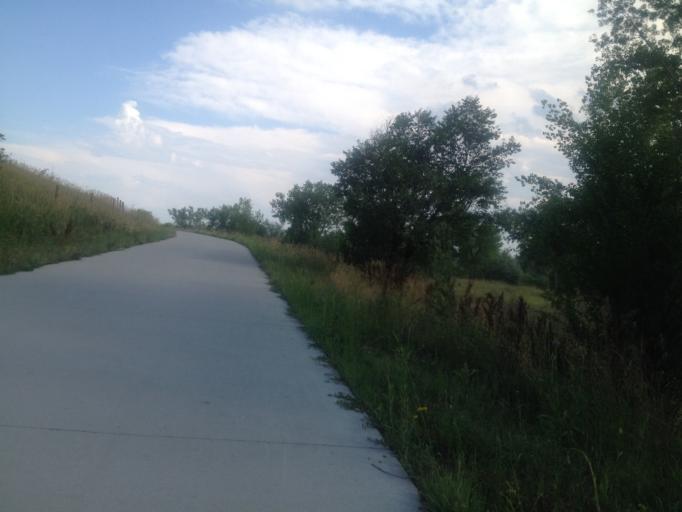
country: US
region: Colorado
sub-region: Boulder County
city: Boulder
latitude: 39.9849
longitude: -105.2328
